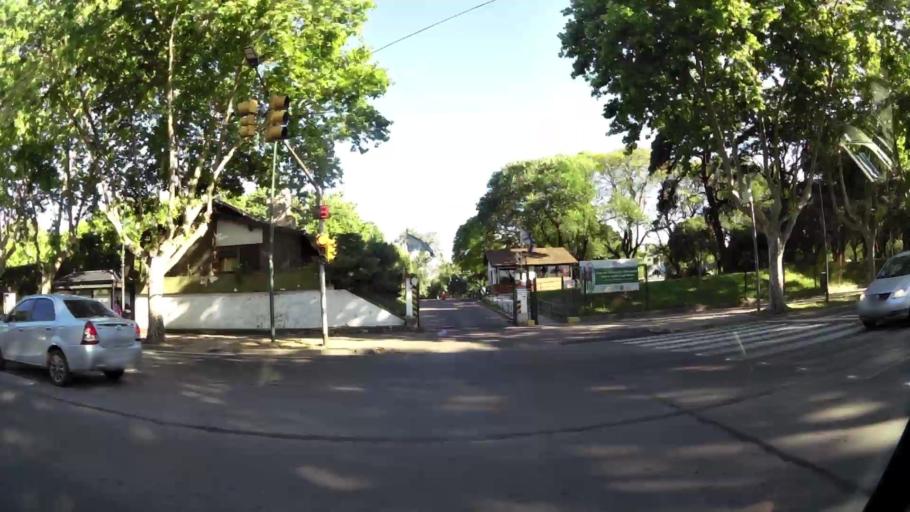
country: AR
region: Buenos Aires
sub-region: Partido de San Isidro
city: San Isidro
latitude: -34.4779
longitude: -58.5196
